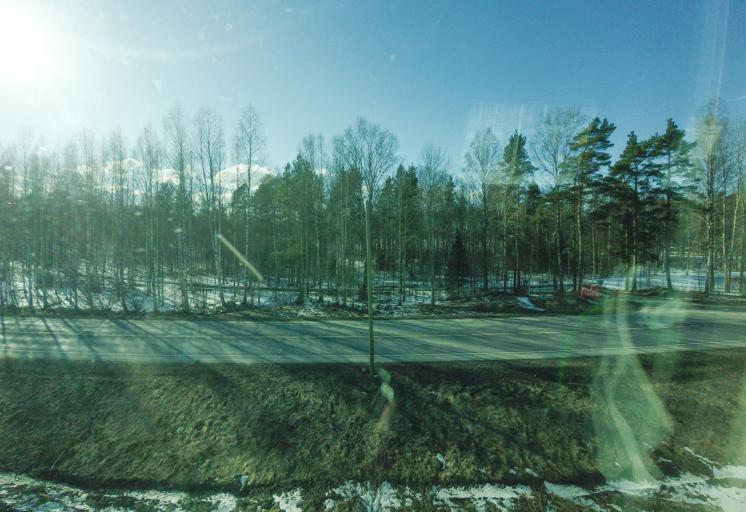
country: FI
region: South Karelia
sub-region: Imatra
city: Parikkala
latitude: 61.5257
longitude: 29.5159
